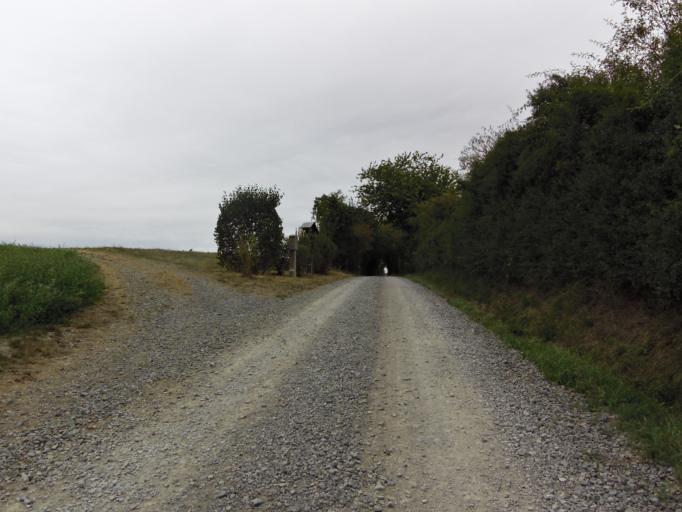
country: DE
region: Bavaria
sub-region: Regierungsbezirk Unterfranken
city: Rimpar
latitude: 49.8284
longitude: 9.9665
